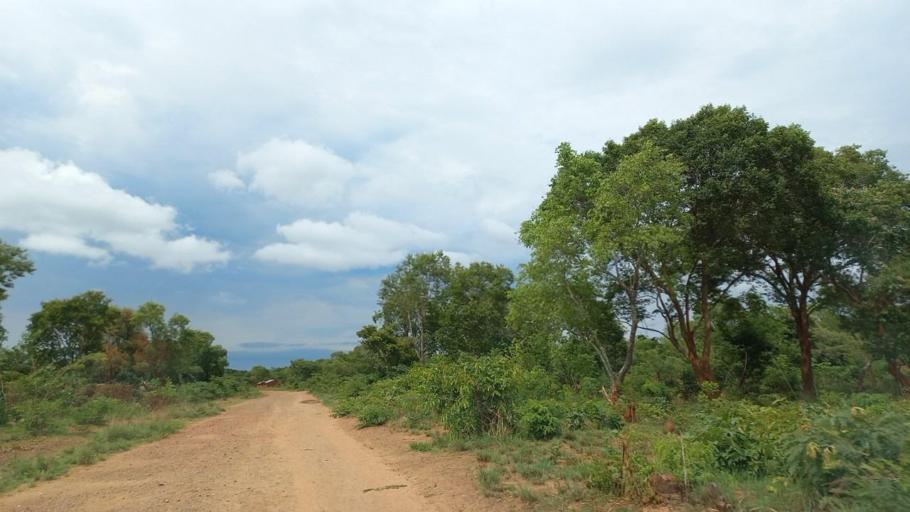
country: ZM
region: North-Western
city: Kalengwa
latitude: -13.4653
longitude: 25.0065
